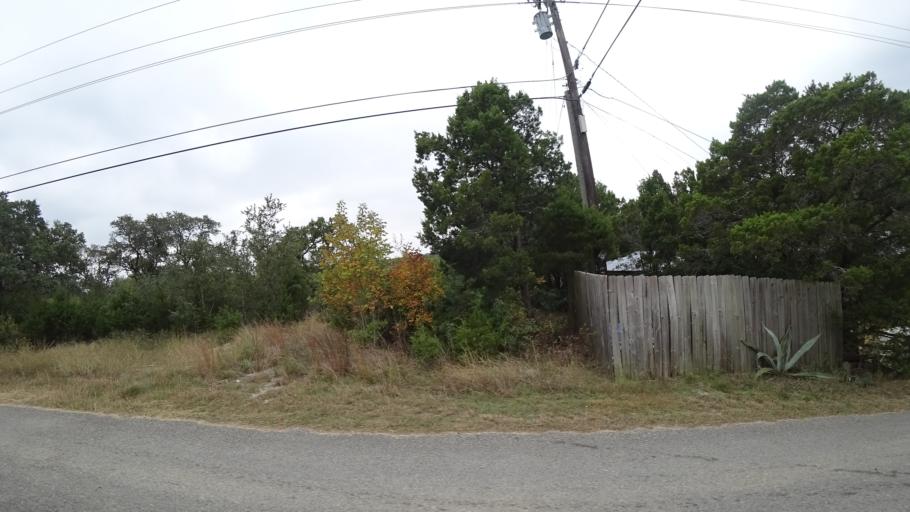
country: US
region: Texas
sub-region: Williamson County
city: Anderson Mill
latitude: 30.4445
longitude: -97.8375
